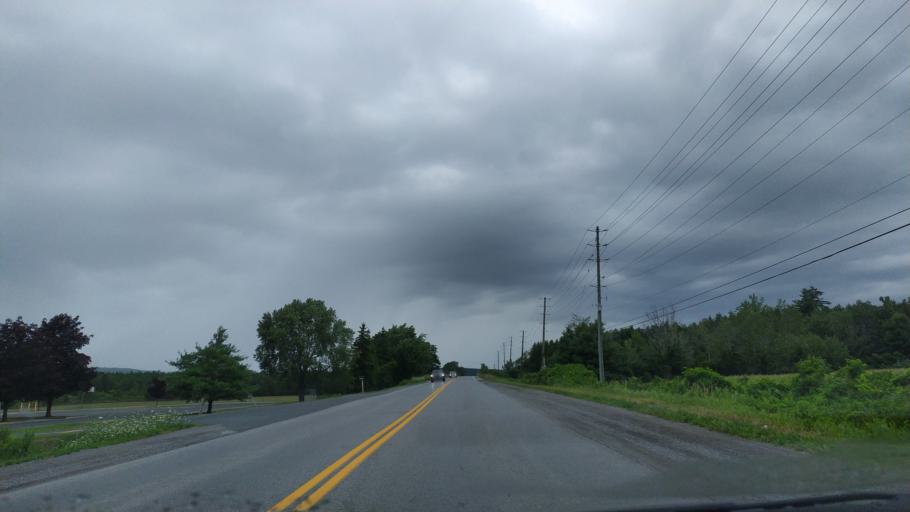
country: CA
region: Ontario
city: Quinte West
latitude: 44.0961
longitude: -77.6147
